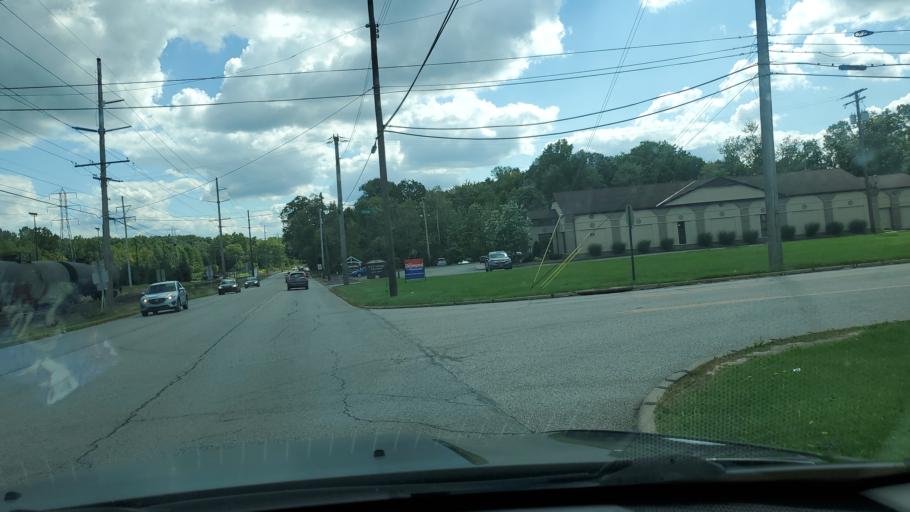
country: US
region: Ohio
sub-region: Mahoning County
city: Boardman
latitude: 41.0212
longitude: -80.6543
